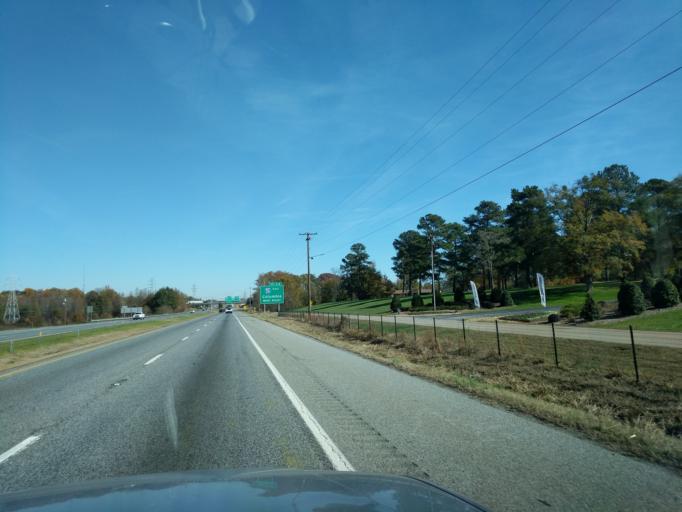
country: US
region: South Carolina
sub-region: Spartanburg County
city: Fairforest
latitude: 34.9657
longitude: -82.0147
